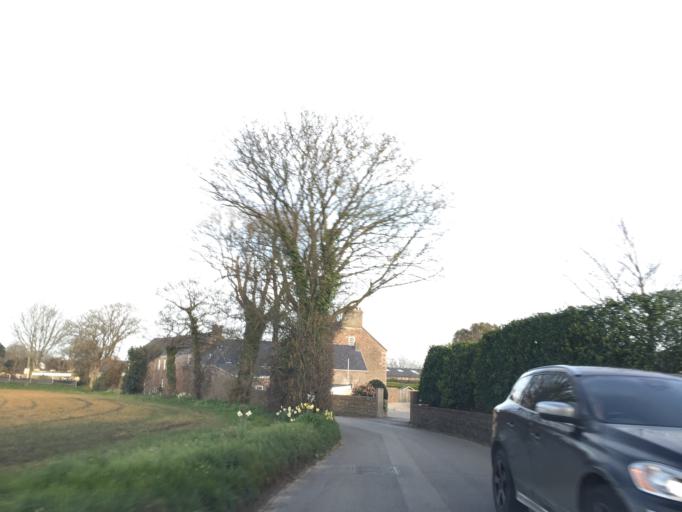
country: JE
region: St Helier
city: Saint Helier
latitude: 49.2280
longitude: -2.0653
